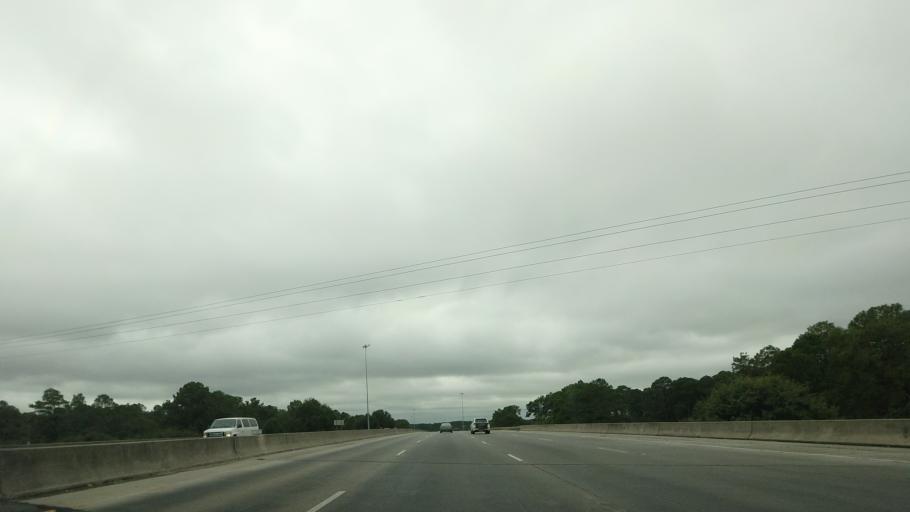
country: US
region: Georgia
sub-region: Tift County
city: Tifton
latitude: 31.4753
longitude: -83.5231
